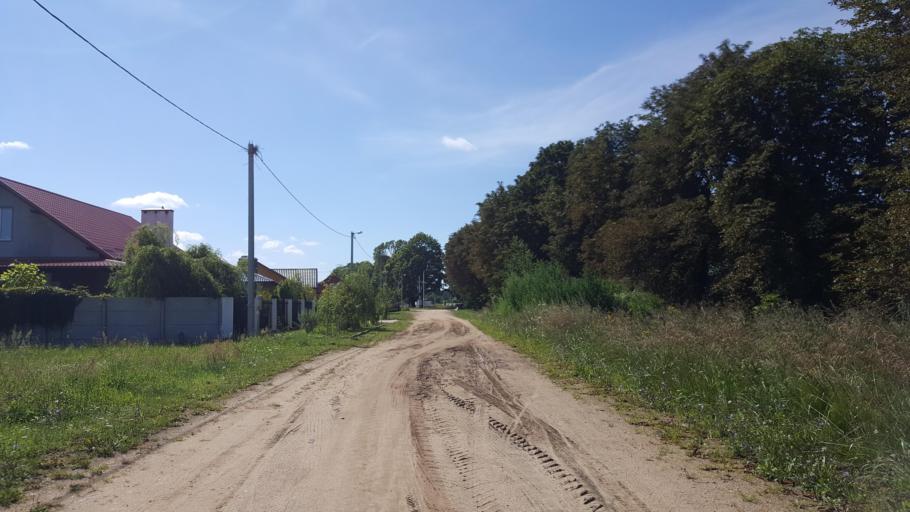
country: BY
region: Brest
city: Charnawchytsy
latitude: 52.2701
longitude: 23.7634
